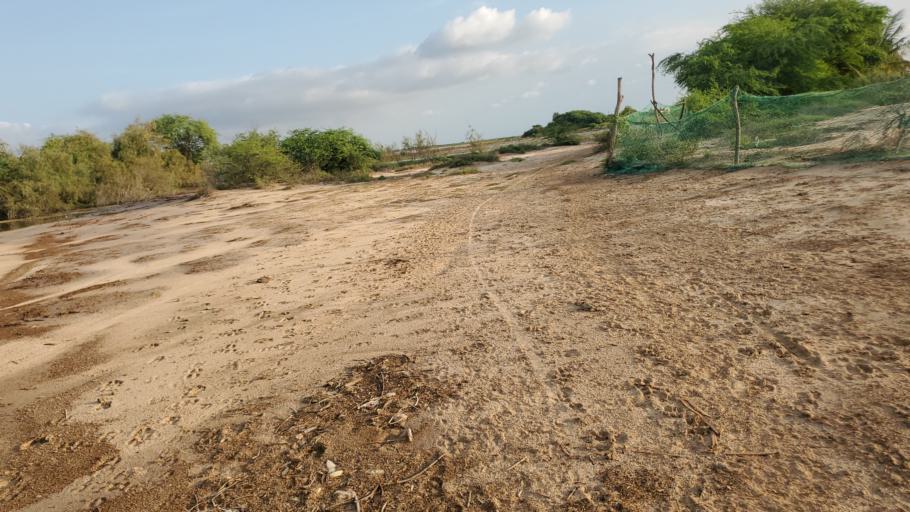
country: SN
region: Saint-Louis
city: Saint-Louis
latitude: 16.0442
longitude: -16.4170
